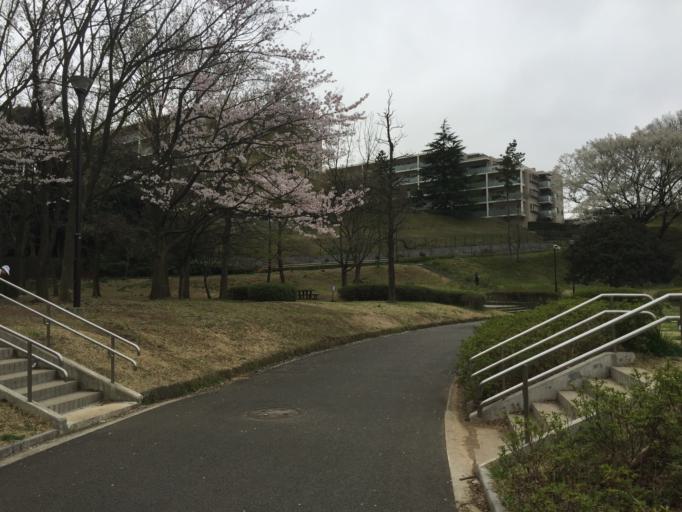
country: JP
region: Kanagawa
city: Yokohama
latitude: 35.4033
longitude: 139.6077
